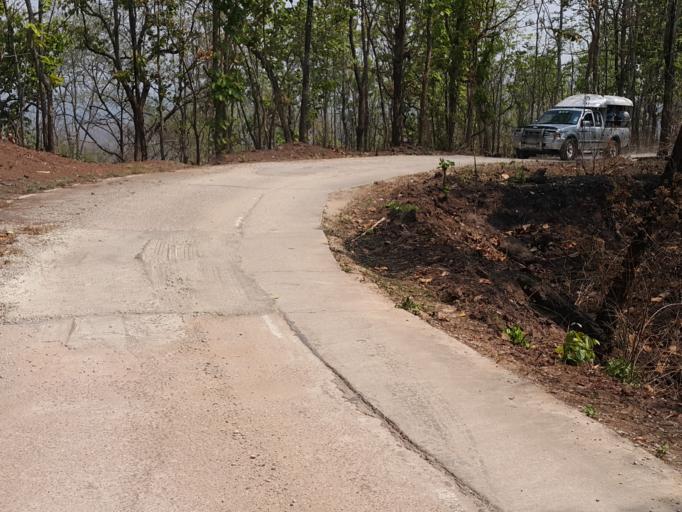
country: TH
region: Lampang
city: Chae Hom
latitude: 18.7491
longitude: 99.5412
